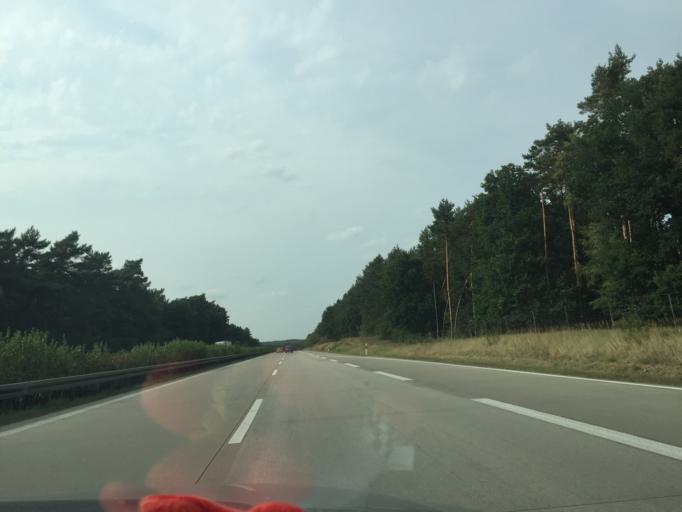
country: DE
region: Brandenburg
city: Bestensee
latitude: 52.2124
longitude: 13.6050
